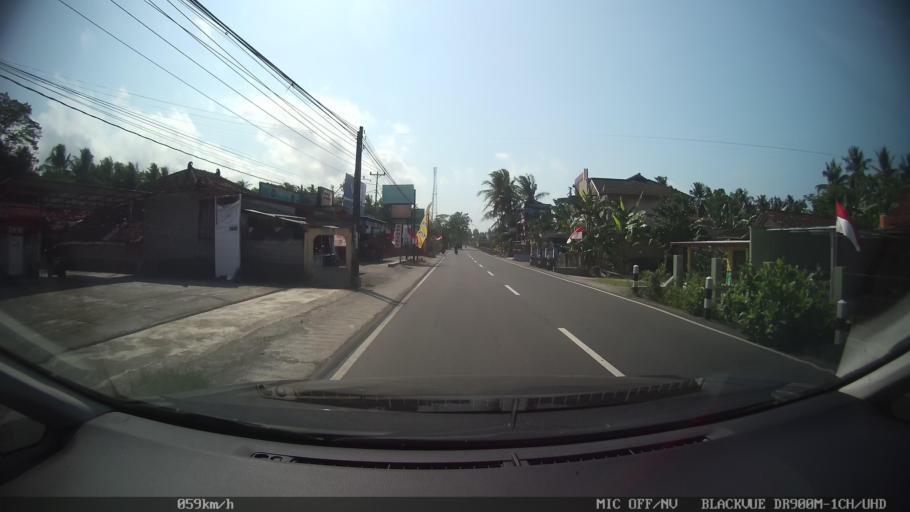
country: ID
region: Daerah Istimewa Yogyakarta
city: Srandakan
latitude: -7.9296
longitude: 110.1986
